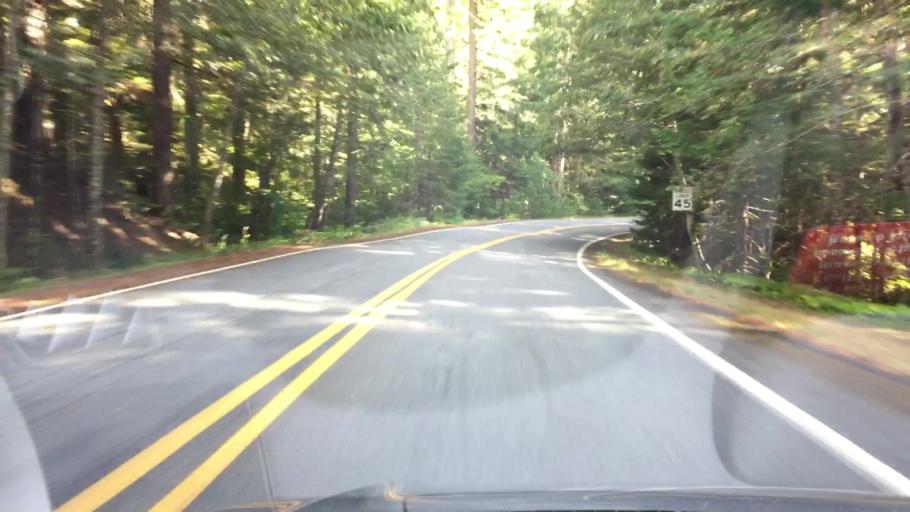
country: US
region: Washington
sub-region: Pierce County
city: Buckley
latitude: 46.7530
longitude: -121.5571
